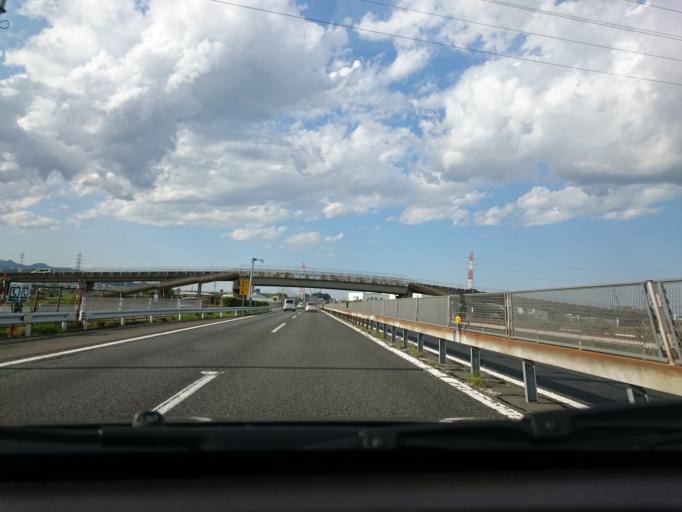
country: JP
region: Kanagawa
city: Isehara
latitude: 35.3972
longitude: 139.3347
